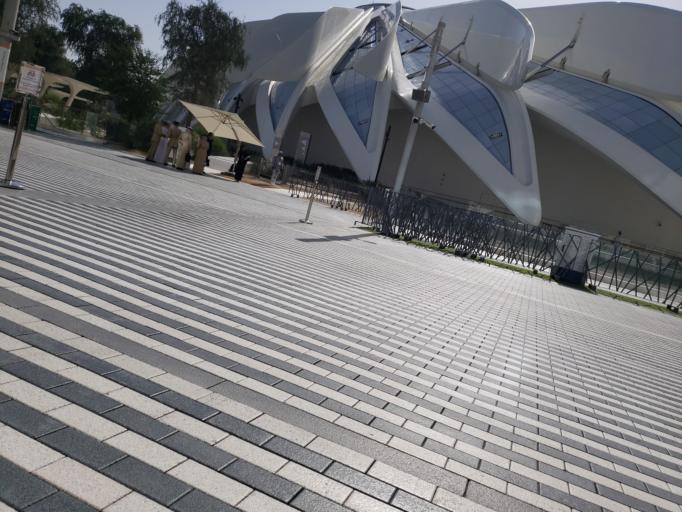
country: AE
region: Dubai
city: Dubai
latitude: 24.9615
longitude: 55.1515
